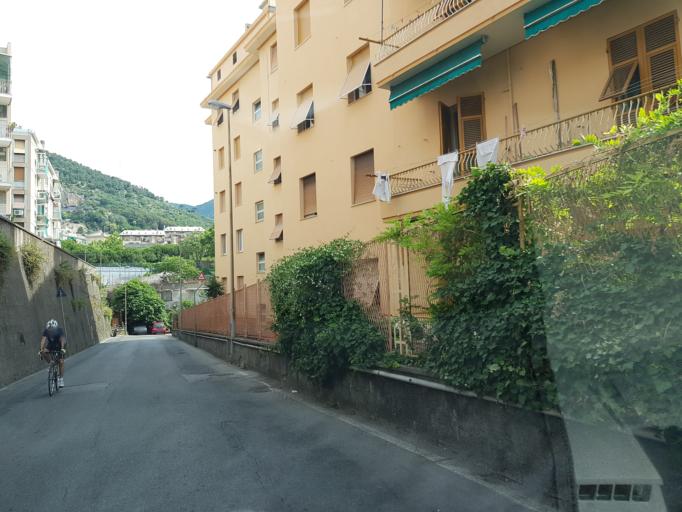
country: IT
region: Liguria
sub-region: Provincia di Genova
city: San Teodoro
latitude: 44.4286
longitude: 8.8463
